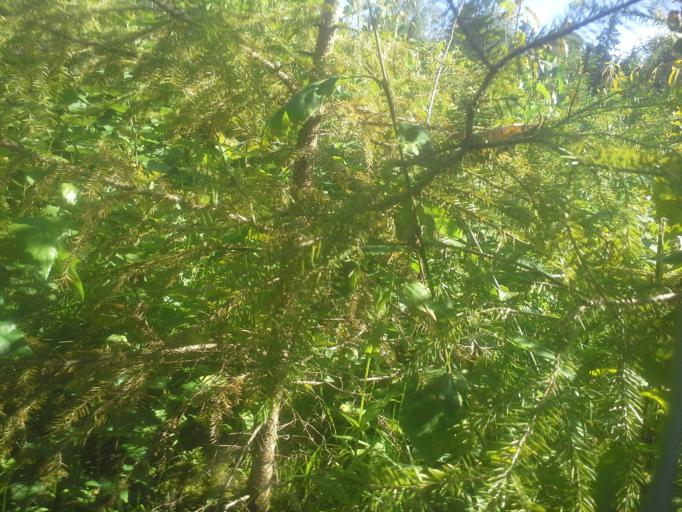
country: RU
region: Moskovskaya
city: Aprelevka
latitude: 55.4635
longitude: 37.0734
